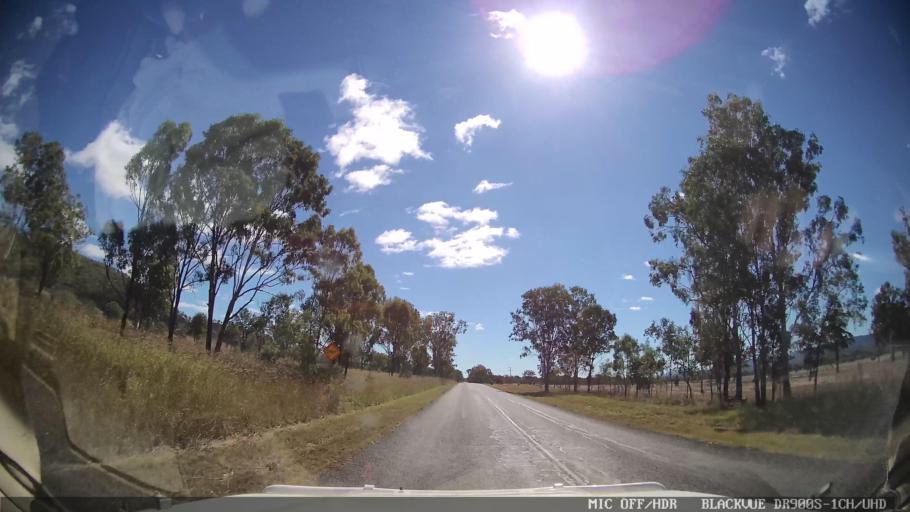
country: AU
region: Queensland
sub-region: Gladstone
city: Toolooa
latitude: -24.4513
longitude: 151.3456
